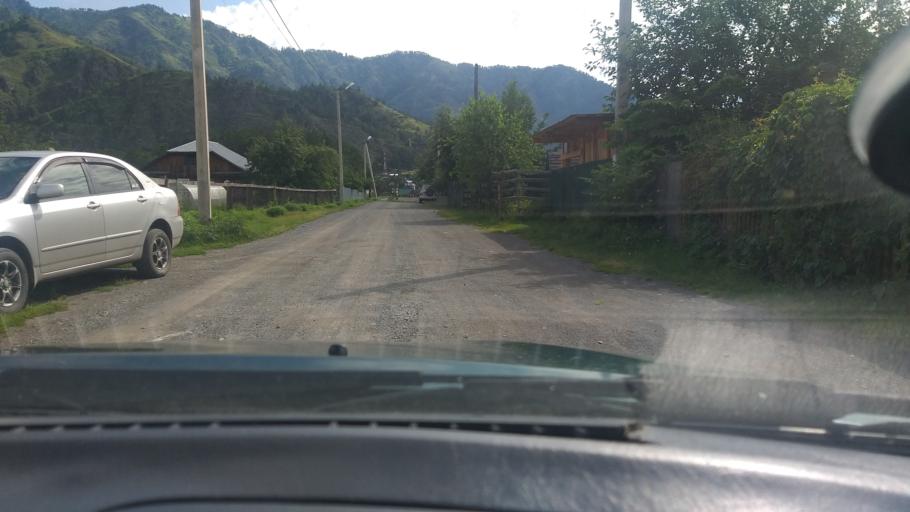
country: RU
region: Altay
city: Chemal
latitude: 51.3905
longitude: 86.0205
